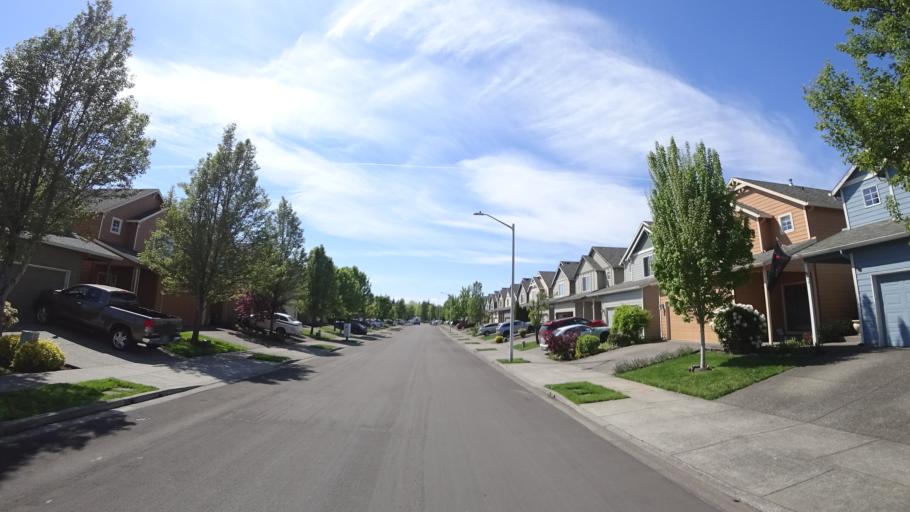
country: US
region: Oregon
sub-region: Washington County
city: Hillsboro
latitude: 45.5067
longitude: -122.9499
